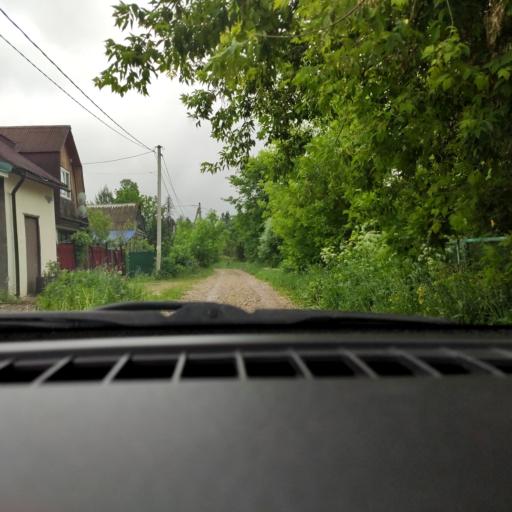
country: RU
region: Perm
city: Froly
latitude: 57.9747
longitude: 56.3069
